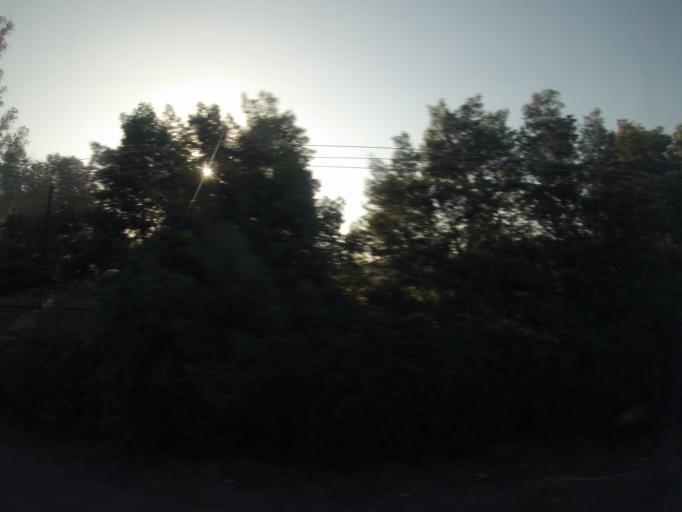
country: CL
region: O'Higgins
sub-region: Provincia de Colchagua
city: Chimbarongo
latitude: -34.6532
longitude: -70.9924
